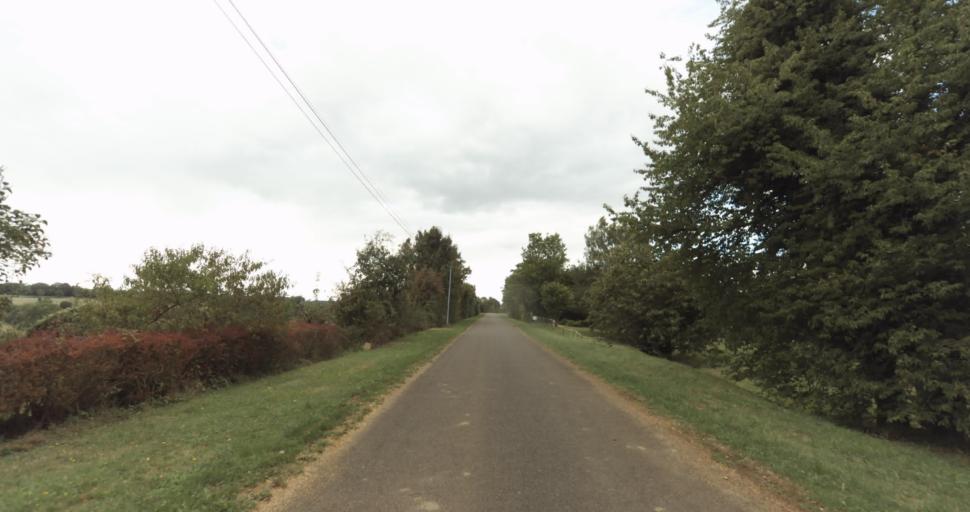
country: FR
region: Lower Normandy
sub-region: Departement de l'Orne
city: Sainte-Gauburge-Sainte-Colombe
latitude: 48.7300
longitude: 0.3944
